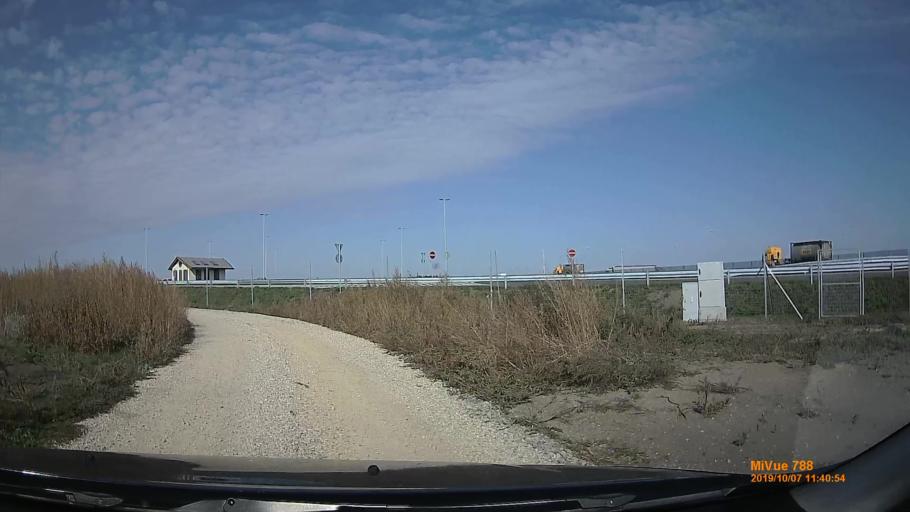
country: HU
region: Bekes
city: Kondoros
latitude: 46.7909
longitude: 20.7063
